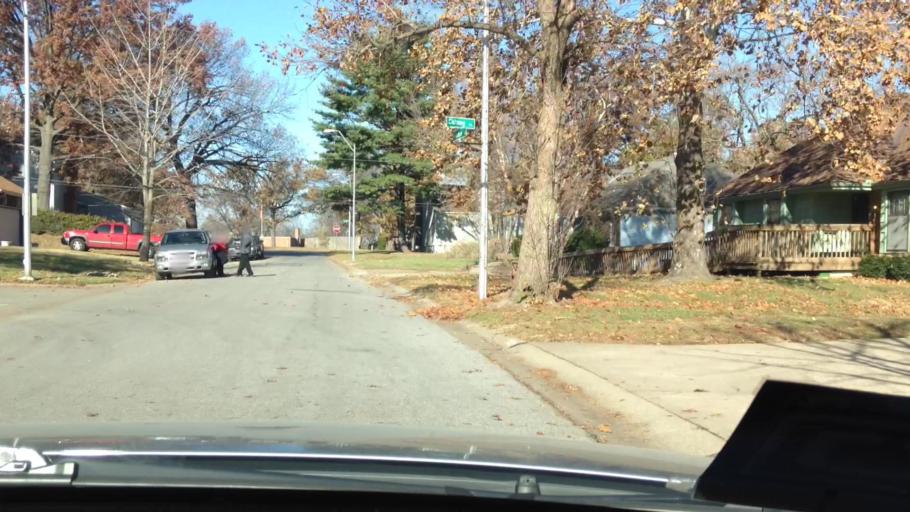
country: US
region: Kansas
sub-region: Johnson County
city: Leawood
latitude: 38.9508
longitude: -94.5689
